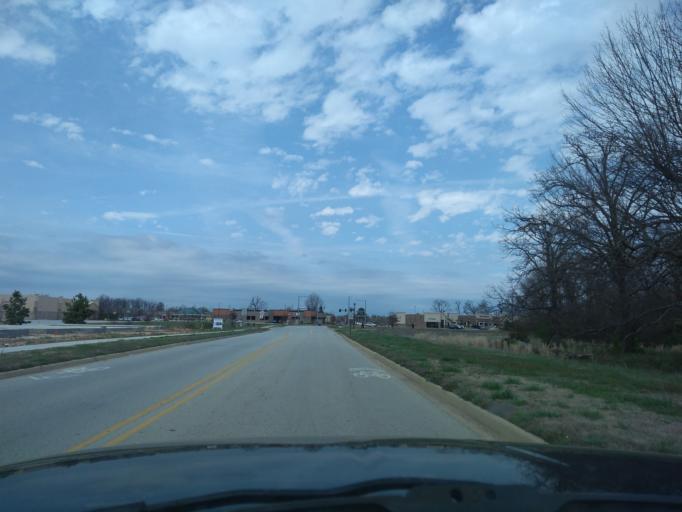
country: US
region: Arkansas
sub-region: Washington County
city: Farmington
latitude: 36.0746
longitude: -94.2088
